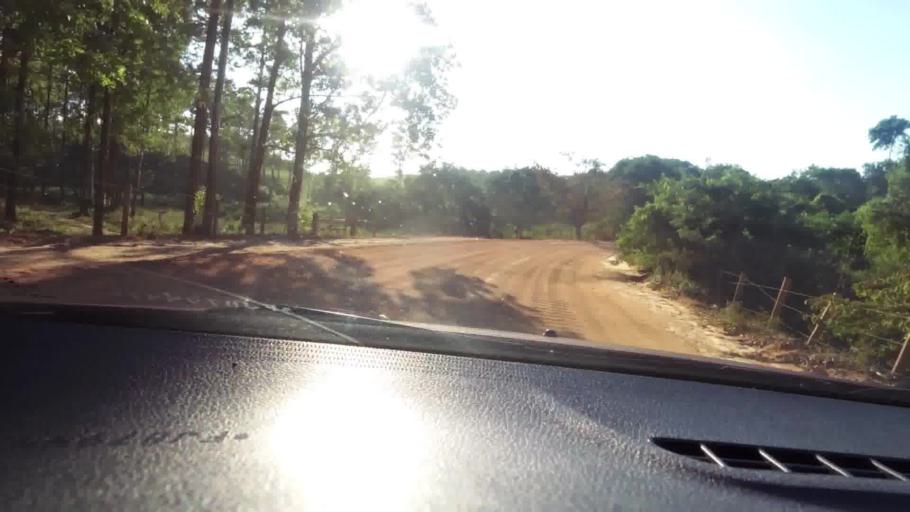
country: BR
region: Espirito Santo
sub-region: Guarapari
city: Guarapari
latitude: -20.5443
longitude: -40.4294
